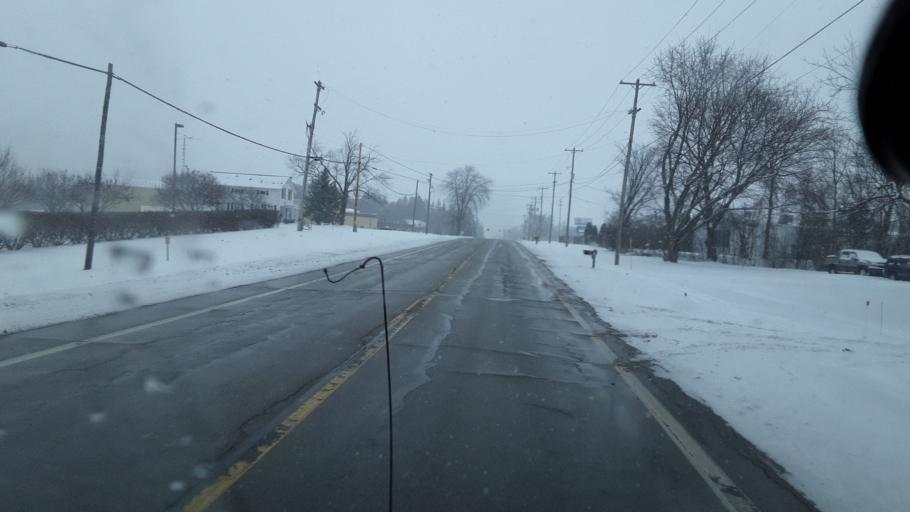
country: US
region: Michigan
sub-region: Jackson County
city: Jackson
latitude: 42.2884
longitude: -84.3990
